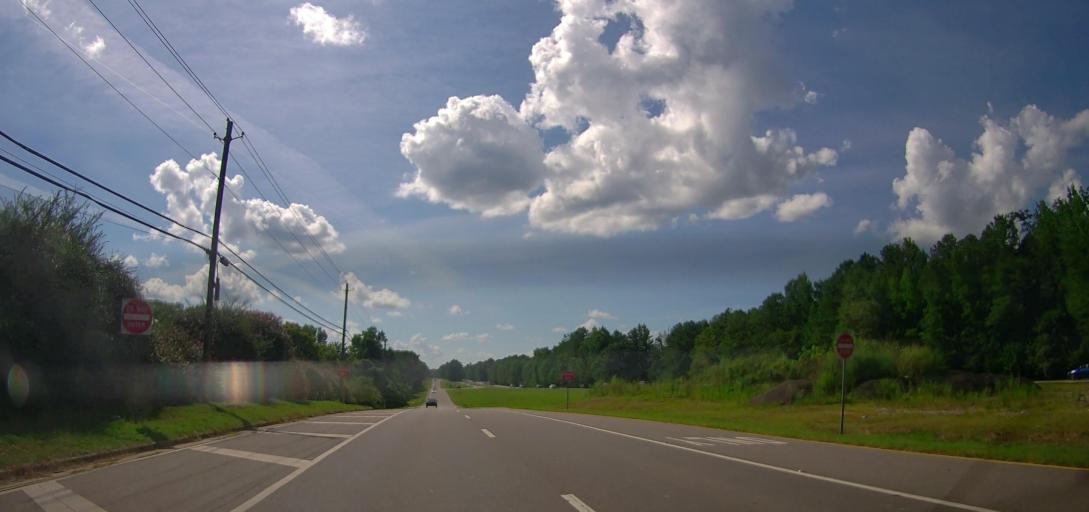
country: US
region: Alabama
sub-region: Tuscaloosa County
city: Northport
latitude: 33.2375
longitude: -87.6557
